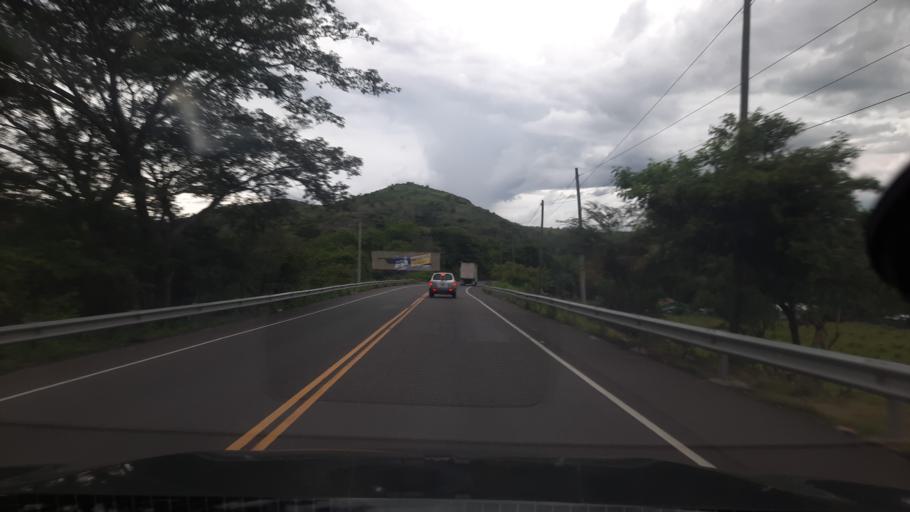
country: HN
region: Choluteca
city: Marcovia
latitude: 13.3528
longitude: -87.2649
